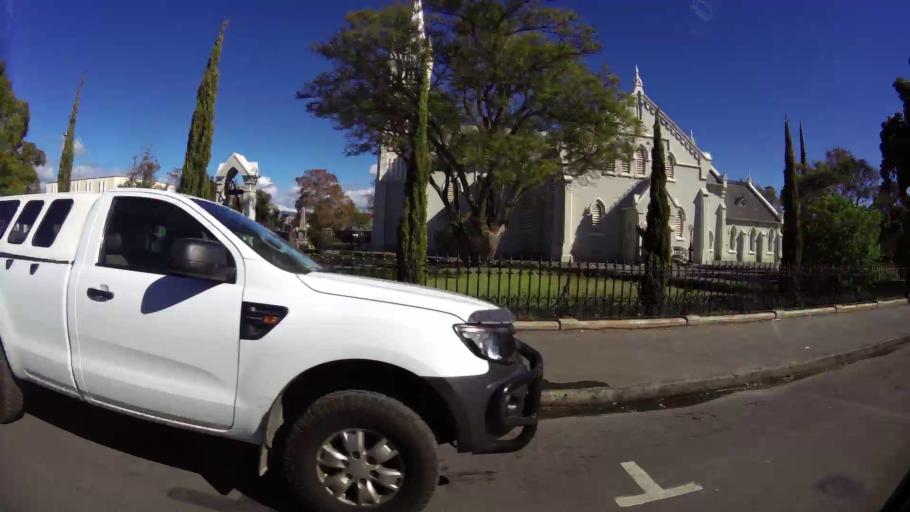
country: ZA
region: Western Cape
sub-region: Cape Winelands District Municipality
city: Ashton
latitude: -33.8031
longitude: 19.8816
